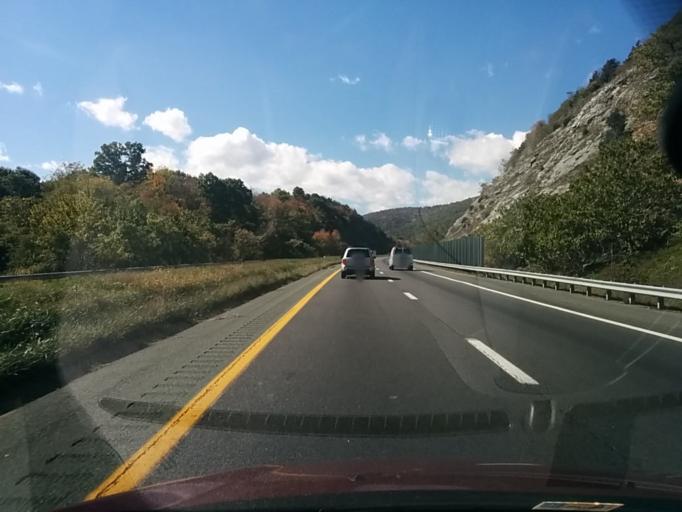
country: US
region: Virginia
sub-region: Augusta County
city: Dooms
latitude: 38.0431
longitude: -78.8034
